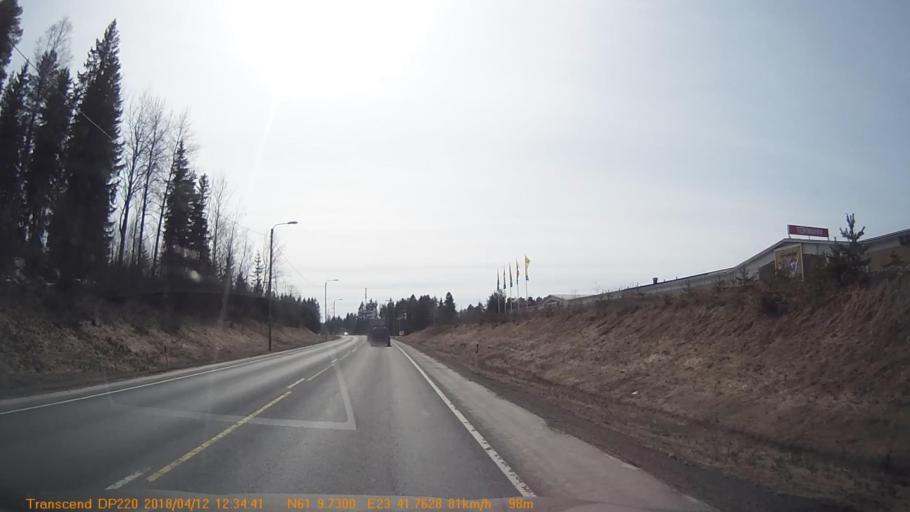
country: FI
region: Pirkanmaa
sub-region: Etelae-Pirkanmaa
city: Kylmaekoski
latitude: 61.1621
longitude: 23.6960
